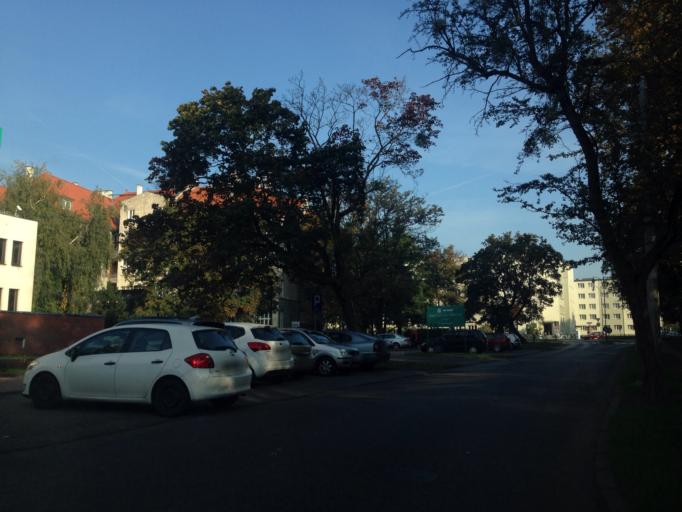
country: PL
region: Kujawsko-Pomorskie
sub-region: Torun
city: Torun
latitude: 53.0109
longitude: 18.5962
